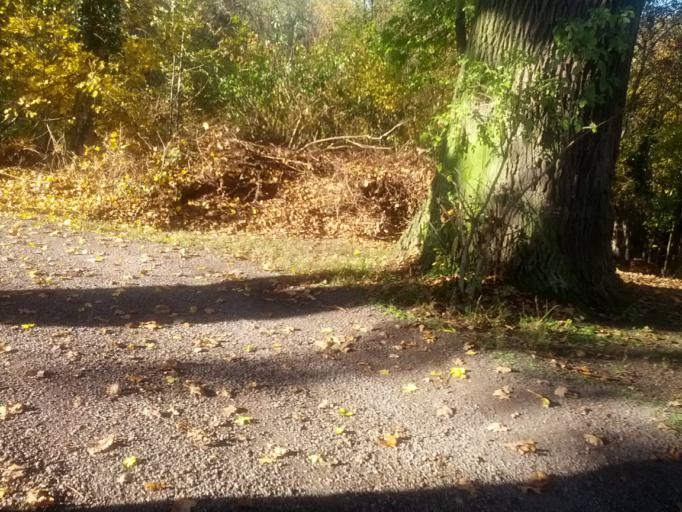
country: DE
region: Thuringia
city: Remstadt
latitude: 50.9567
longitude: 10.6669
